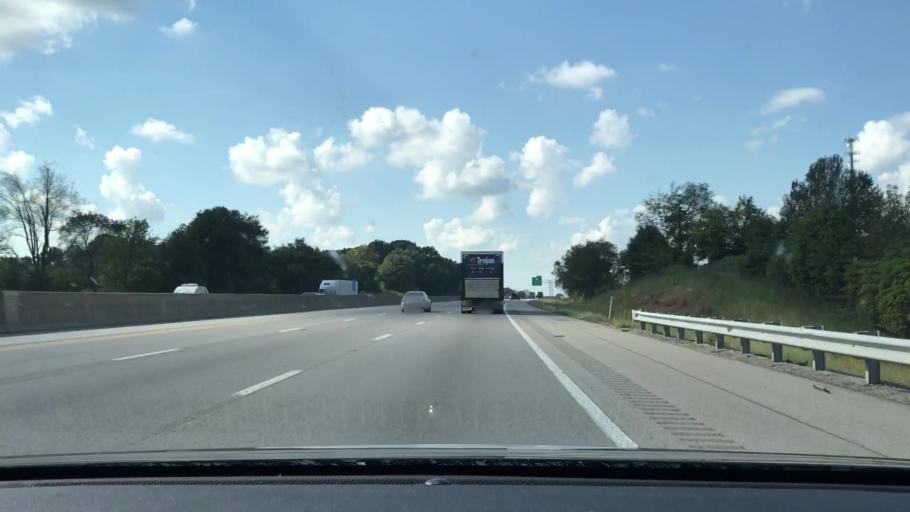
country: US
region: Kentucky
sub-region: Simpson County
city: Franklin
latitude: 36.7444
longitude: -86.4971
